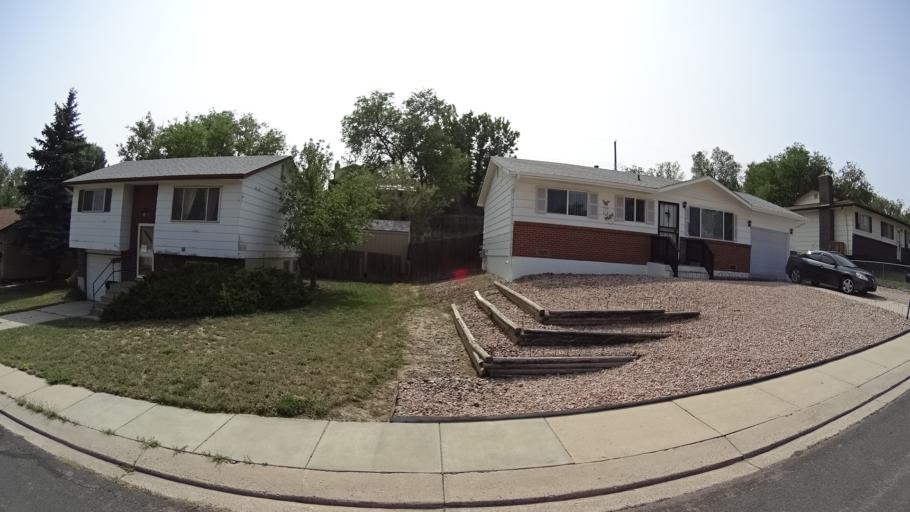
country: US
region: Colorado
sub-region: El Paso County
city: Stratmoor
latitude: 38.8007
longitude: -104.7716
